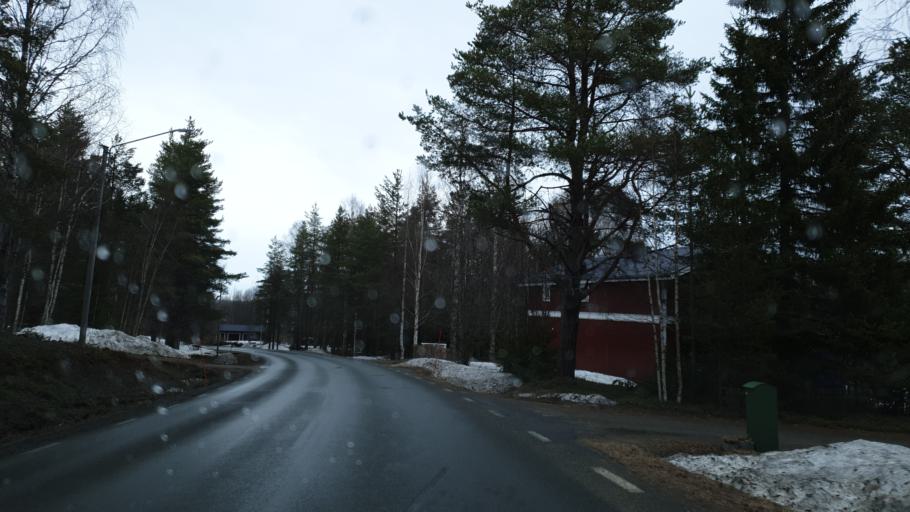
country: SE
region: Vaesterbotten
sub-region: Skelleftea Kommun
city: Kage
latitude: 64.8267
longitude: 20.9866
